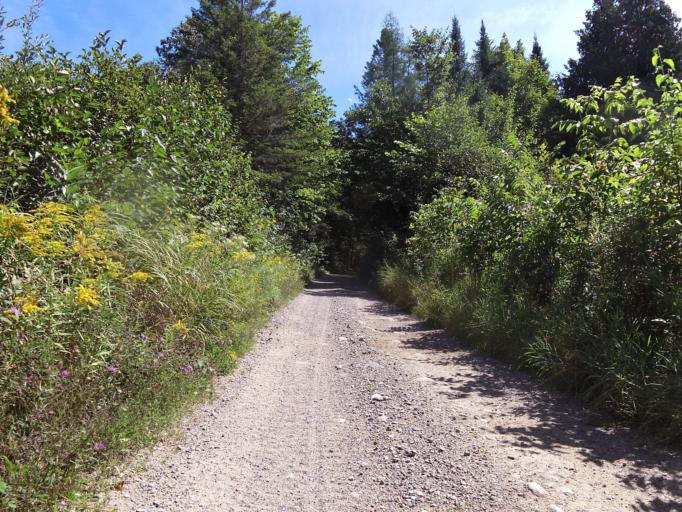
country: CA
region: Ontario
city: Renfrew
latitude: 45.0194
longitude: -76.7015
